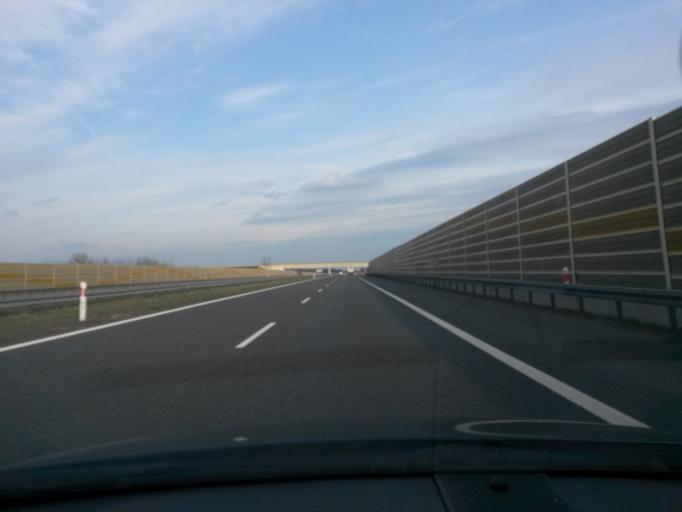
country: PL
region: Lodz Voivodeship
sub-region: Powiat zgierski
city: Parzeczew
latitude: 51.9383
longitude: 19.2439
